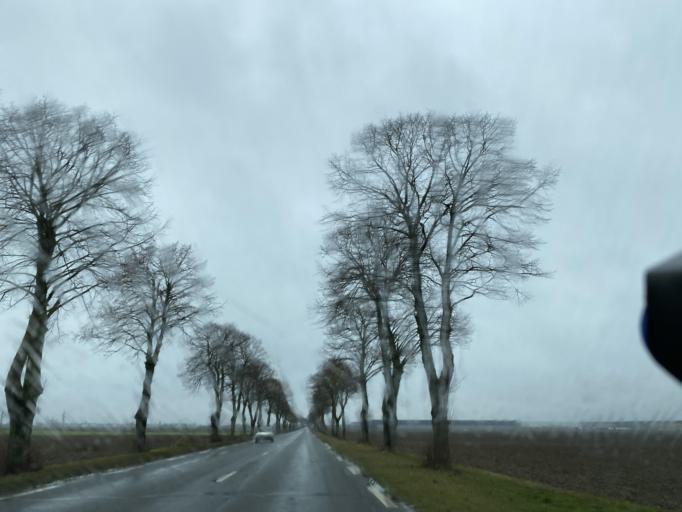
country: FR
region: Centre
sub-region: Departement du Loiret
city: Artenay
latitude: 48.1011
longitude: 1.8646
